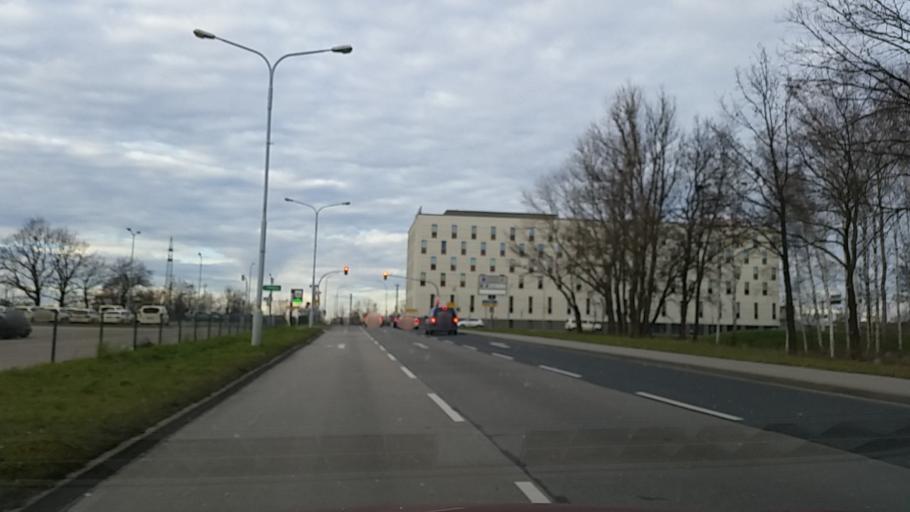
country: DE
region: Brandenburg
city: Schonefeld
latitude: 52.3909
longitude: 13.5187
